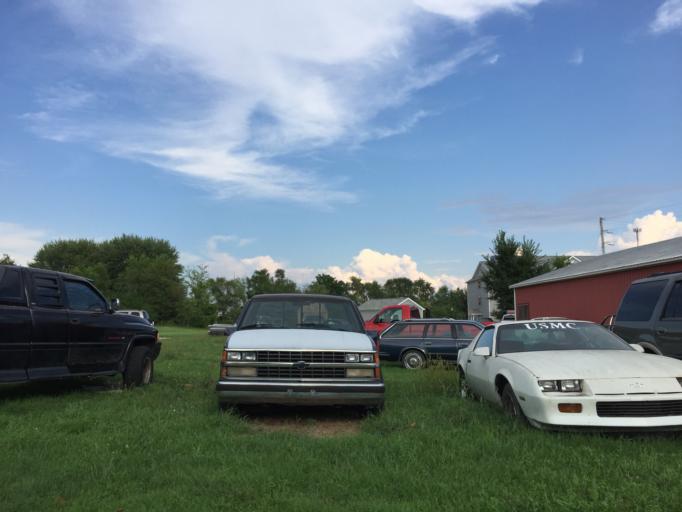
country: US
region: Indiana
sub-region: Howard County
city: Kokomo
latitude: 40.4709
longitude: -86.1138
